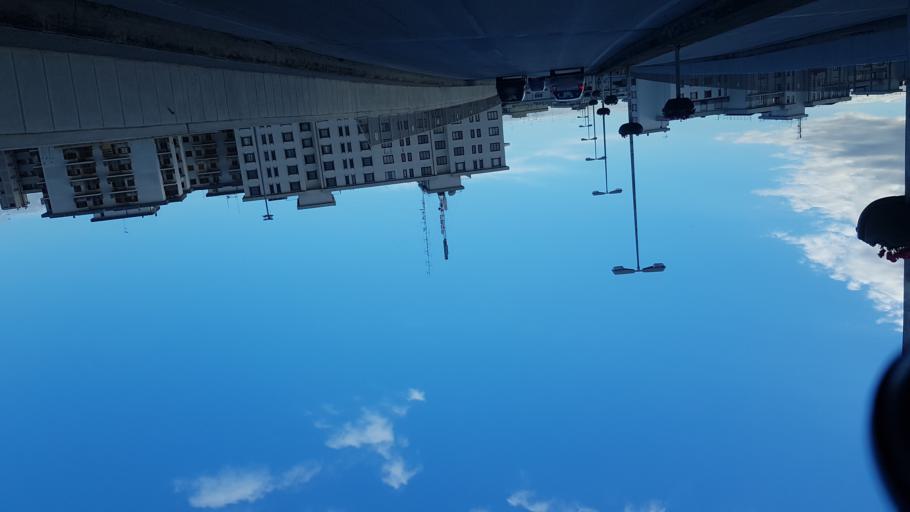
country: IT
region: Apulia
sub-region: Provincia di Brindisi
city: Brindisi
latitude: 40.6323
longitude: 17.9414
